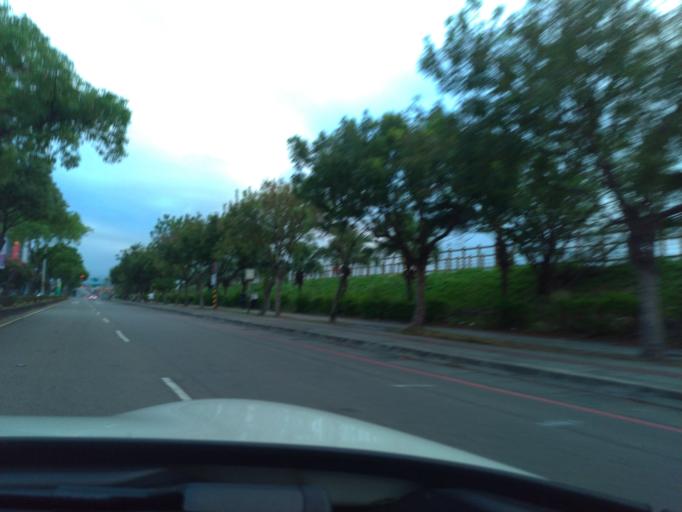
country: TW
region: Taiwan
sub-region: Hsinchu
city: Zhubei
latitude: 24.8022
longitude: 121.0334
